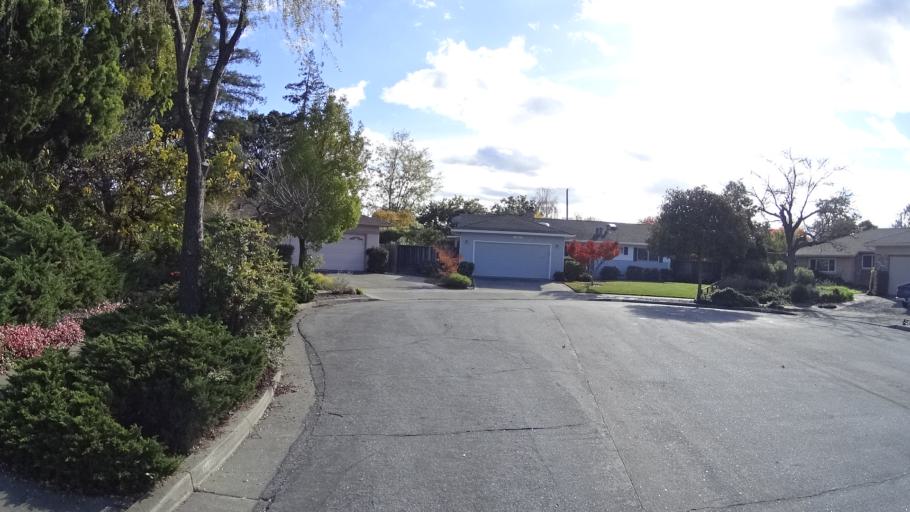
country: US
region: California
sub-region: Santa Clara County
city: Sunnyvale
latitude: 37.3443
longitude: -122.0541
